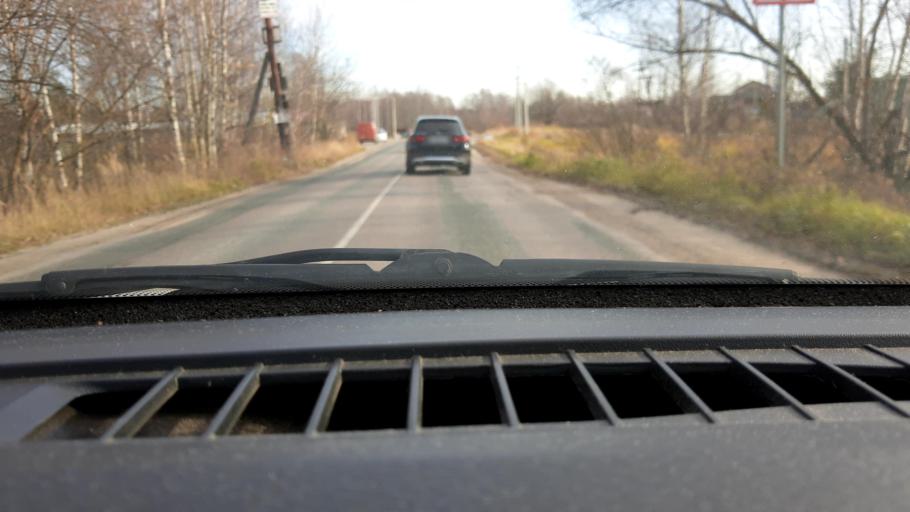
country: RU
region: Nizjnij Novgorod
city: Neklyudovo
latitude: 56.4383
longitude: 43.9165
